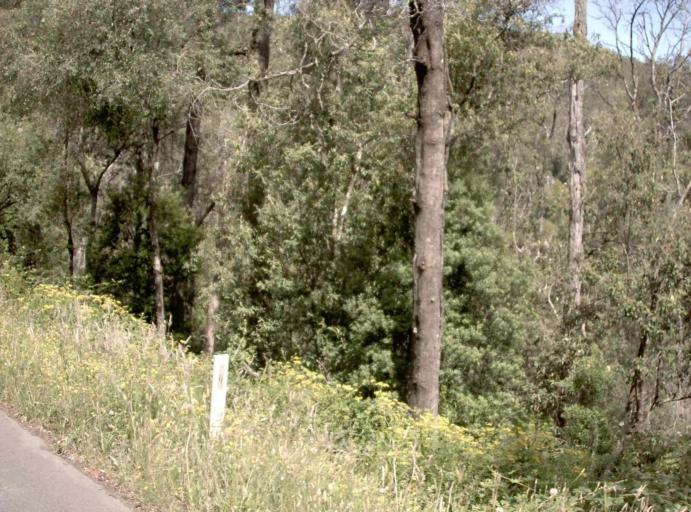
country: AU
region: Victoria
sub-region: Latrobe
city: Moe
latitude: -37.8226
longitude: 146.1657
